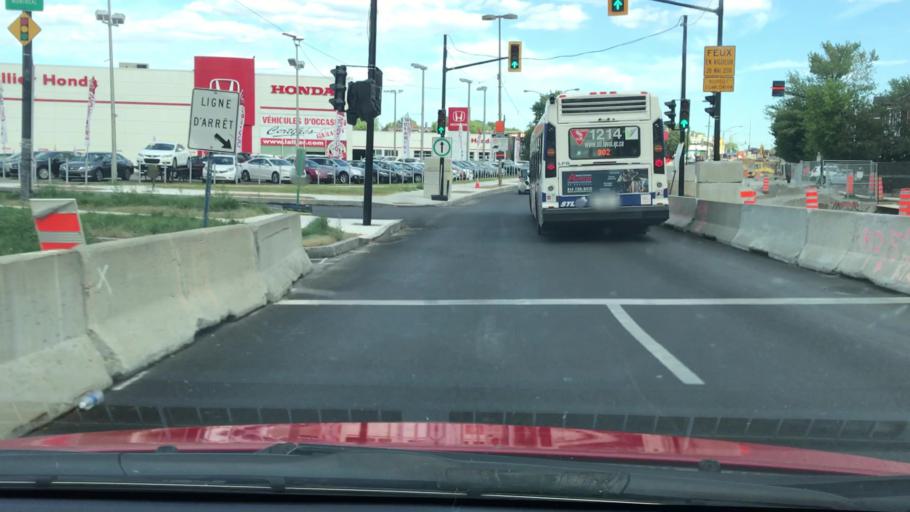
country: CA
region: Quebec
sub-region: Laval
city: Laval
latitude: 45.5314
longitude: -73.7261
